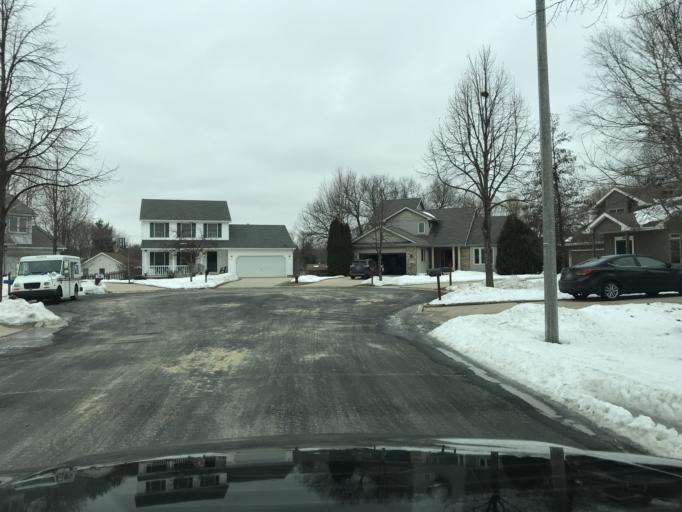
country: US
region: Wisconsin
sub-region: Dane County
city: Monona
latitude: 43.0725
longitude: -89.2839
